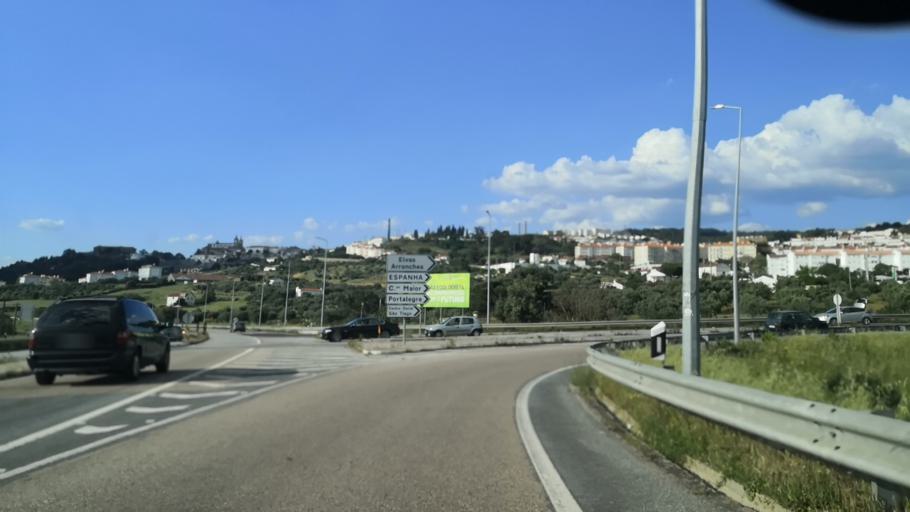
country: PT
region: Portalegre
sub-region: Portalegre
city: Portalegre
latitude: 39.2786
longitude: -7.4342
